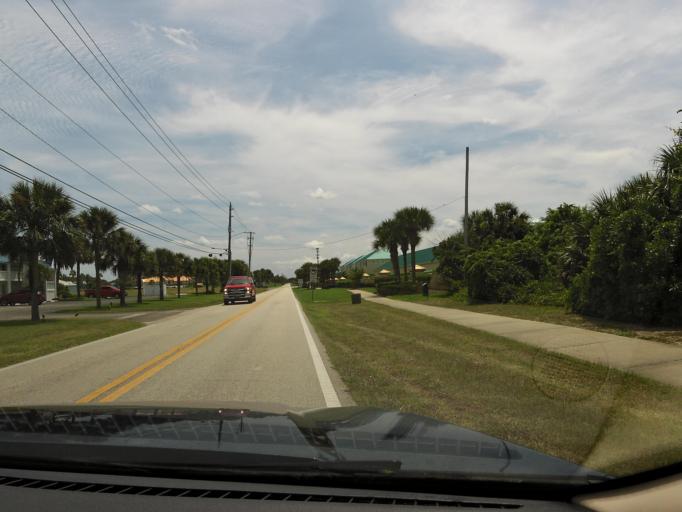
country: US
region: Florida
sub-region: Volusia County
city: Ponce Inlet
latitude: 29.1044
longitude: -80.9439
